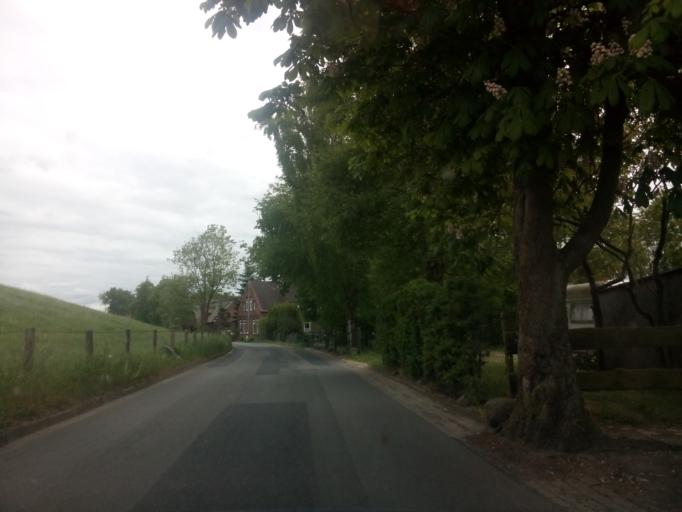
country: DE
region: Lower Saxony
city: Lemwerder
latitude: 53.1689
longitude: 8.5770
